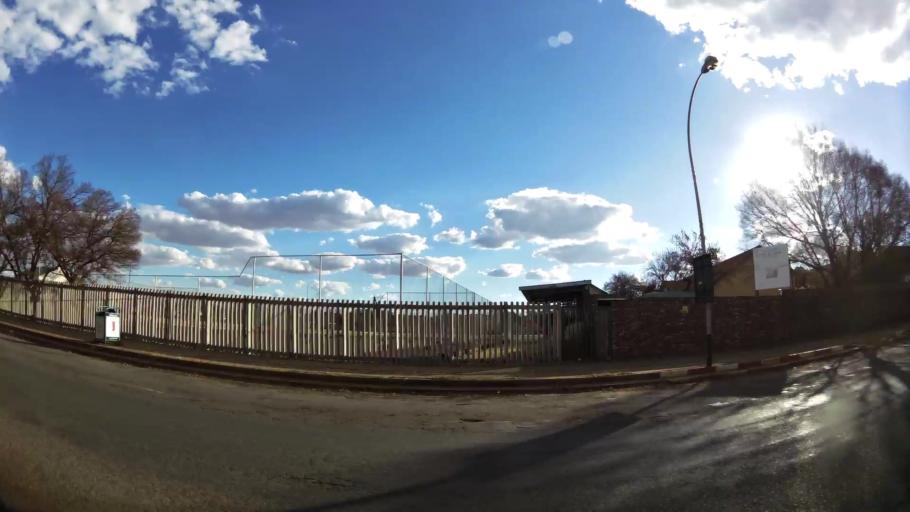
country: ZA
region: North-West
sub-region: Dr Kenneth Kaunda District Municipality
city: Potchefstroom
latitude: -26.6985
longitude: 27.0981
